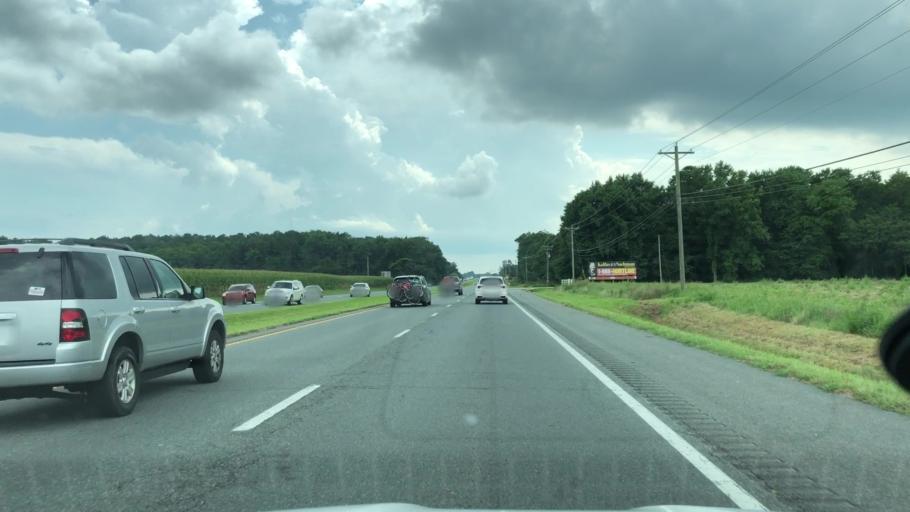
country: US
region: Virginia
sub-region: Accomack County
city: Accomac
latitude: 37.7963
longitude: -75.6006
